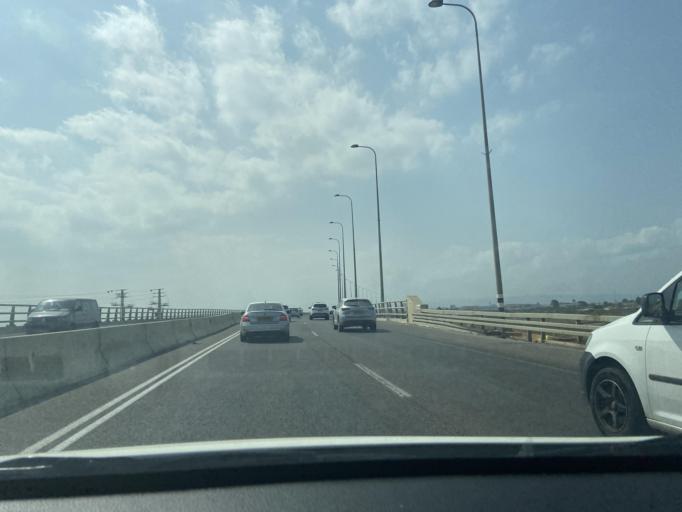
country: IL
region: Northern District
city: `Akko
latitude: 32.9135
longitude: 35.0962
